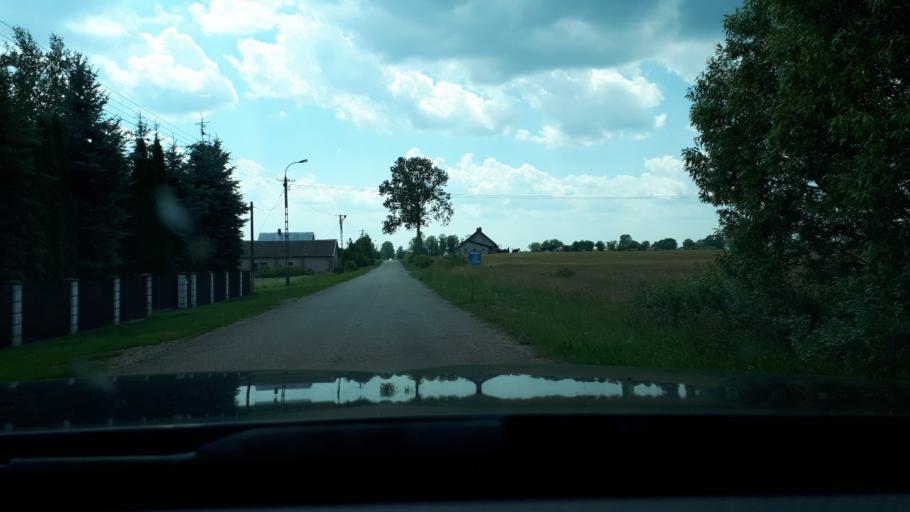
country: PL
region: Podlasie
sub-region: Powiat bialostocki
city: Lapy
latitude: 53.0888
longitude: 22.8411
